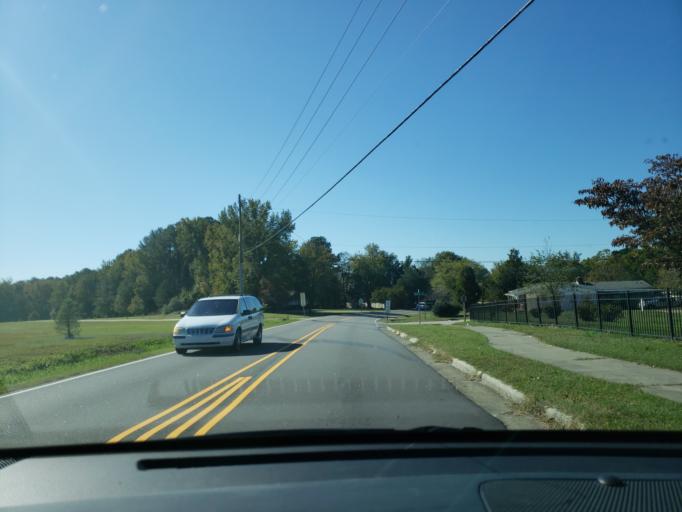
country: US
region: North Carolina
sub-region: Wake County
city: Raleigh
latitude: 35.8197
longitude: -78.5754
